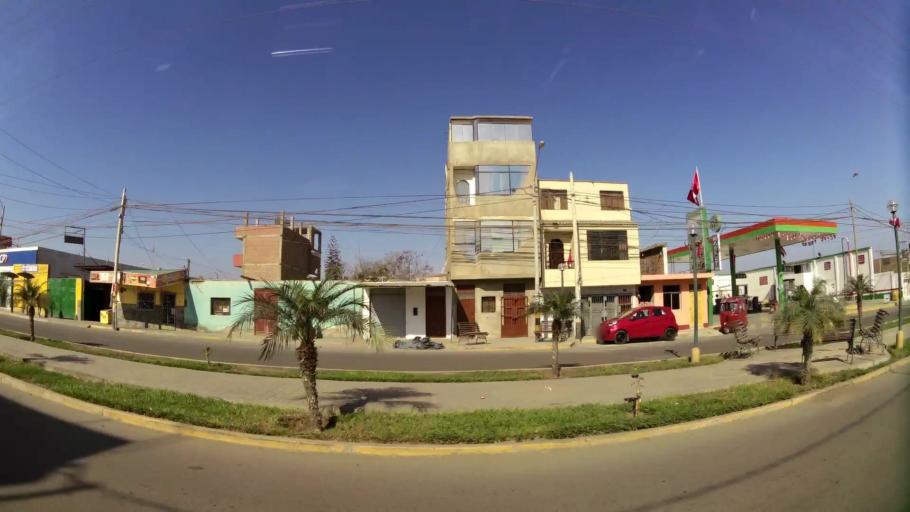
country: PE
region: Ica
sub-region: Provincia de Chincha
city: Chincha Alta
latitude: -13.4052
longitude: -76.1299
